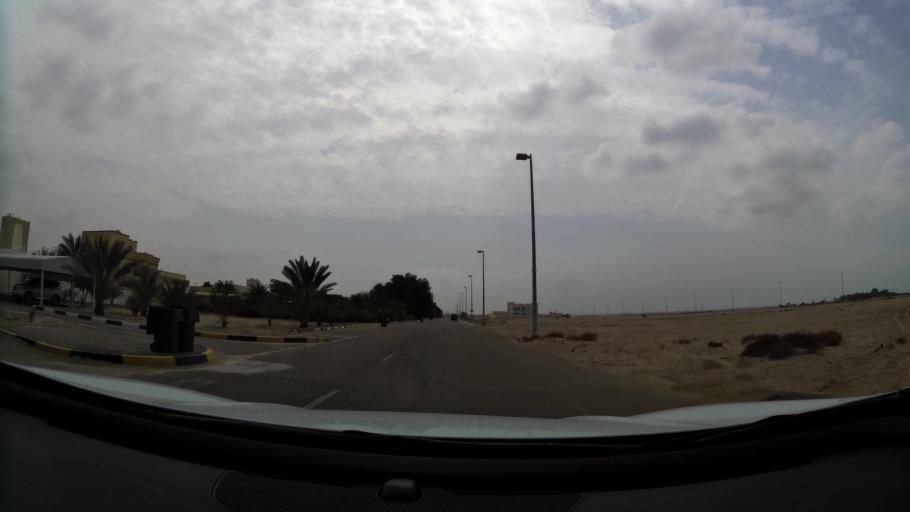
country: AE
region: Abu Dhabi
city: Abu Dhabi
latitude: 24.6101
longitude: 54.6424
